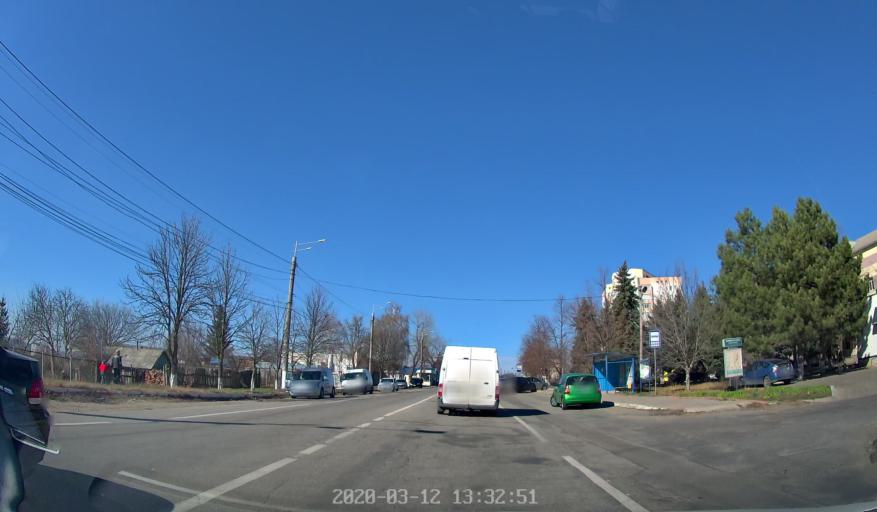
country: MD
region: Laloveni
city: Ialoveni
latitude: 46.9534
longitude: 28.7704
